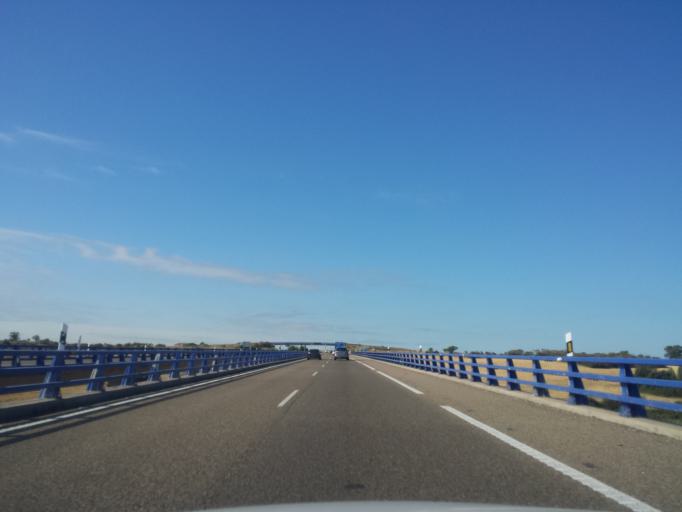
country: ES
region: Castille and Leon
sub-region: Provincia de Leon
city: Villamanan
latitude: 42.3443
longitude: -5.6051
